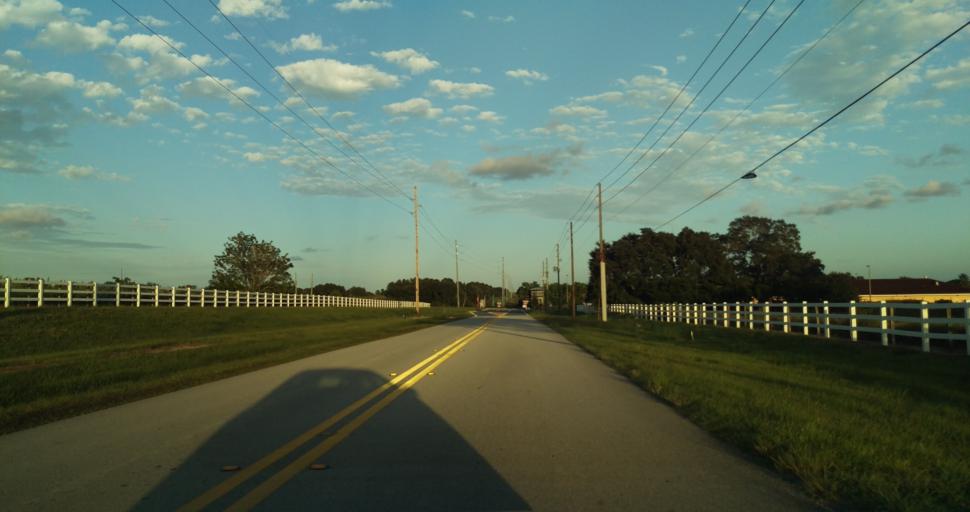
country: US
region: Florida
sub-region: Orange County
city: Lake Butler
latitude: 28.4416
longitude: -81.6265
